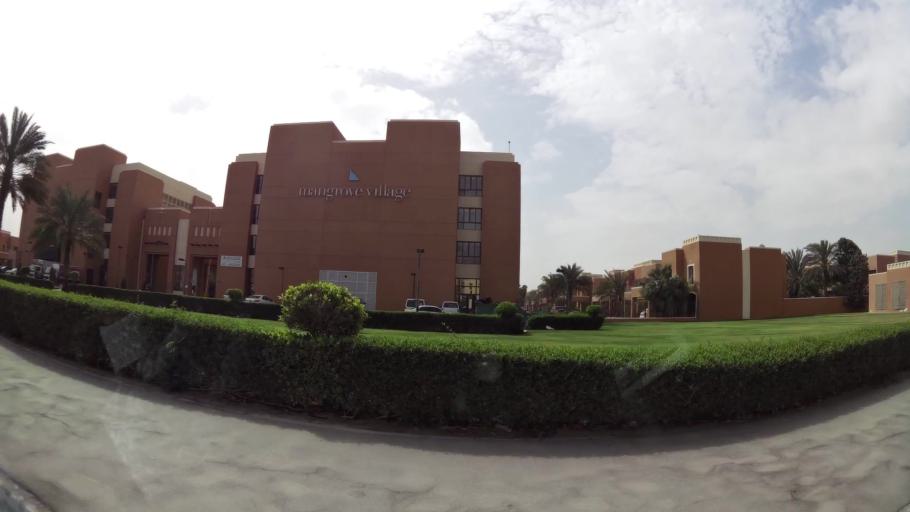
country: AE
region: Abu Dhabi
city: Abu Dhabi
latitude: 24.3938
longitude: 54.4934
